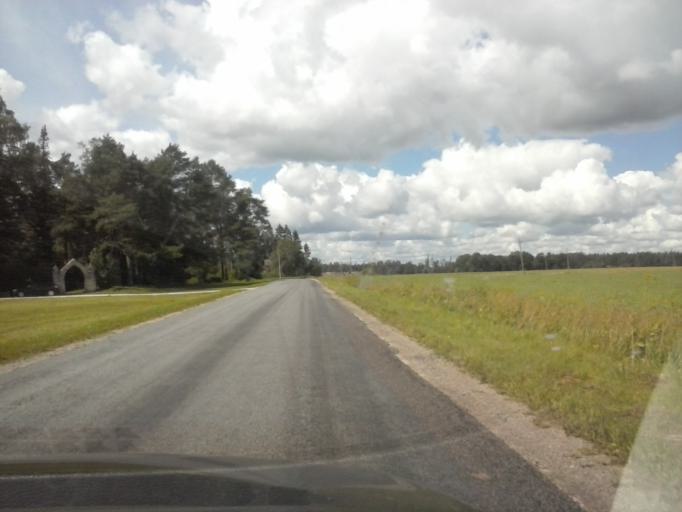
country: EE
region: Laeaene-Virumaa
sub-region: Rakke vald
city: Rakke
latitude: 59.0488
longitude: 26.3785
